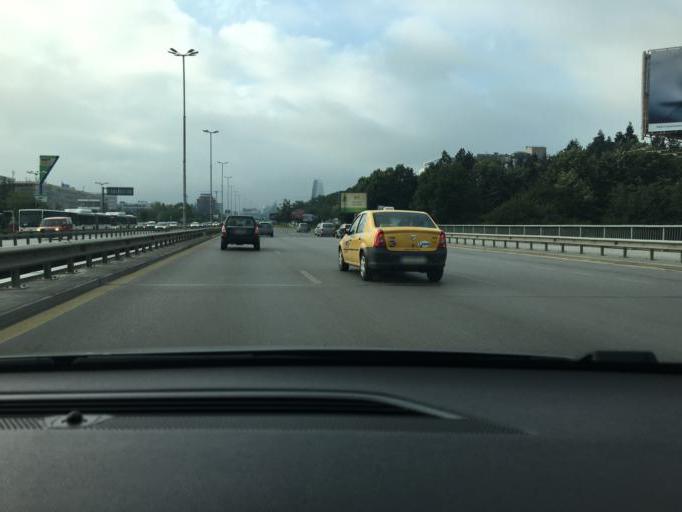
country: BG
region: Sofia-Capital
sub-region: Stolichna Obshtina
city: Sofia
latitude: 42.6573
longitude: 23.3842
